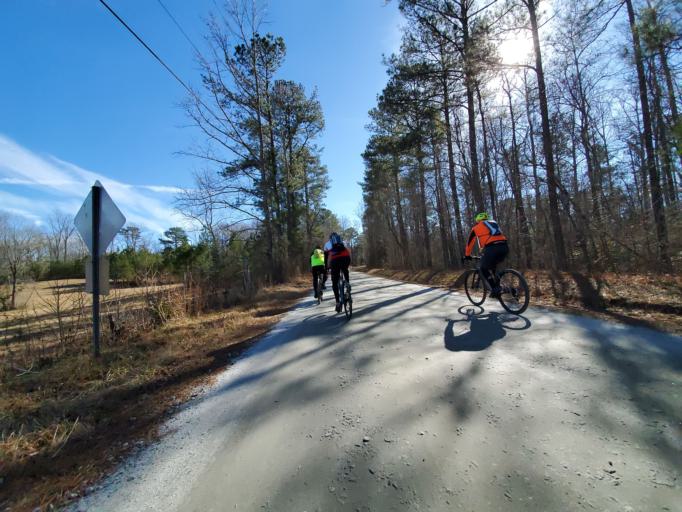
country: US
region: Georgia
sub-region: Fulton County
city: Chattahoochee Hills
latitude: 33.5756
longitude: -84.7823
